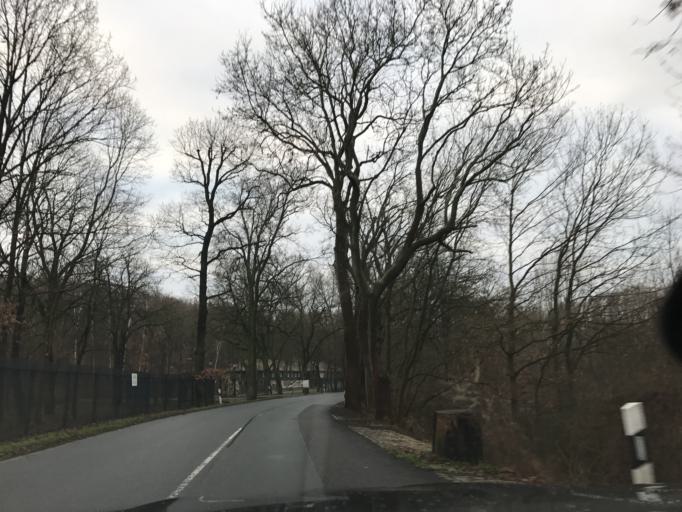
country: DE
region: Brandenburg
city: Werder
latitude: 52.3891
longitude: 12.9743
